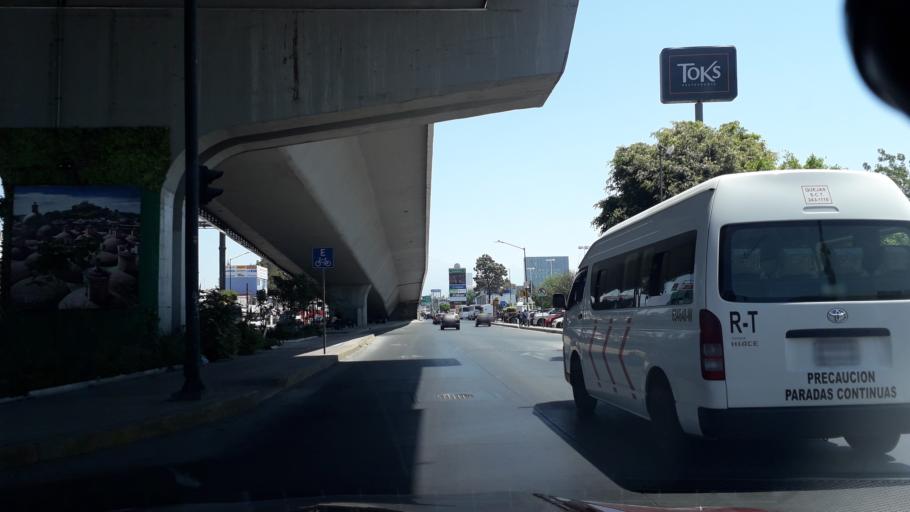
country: MX
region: Puebla
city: Puebla
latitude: 19.0645
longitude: -98.1797
